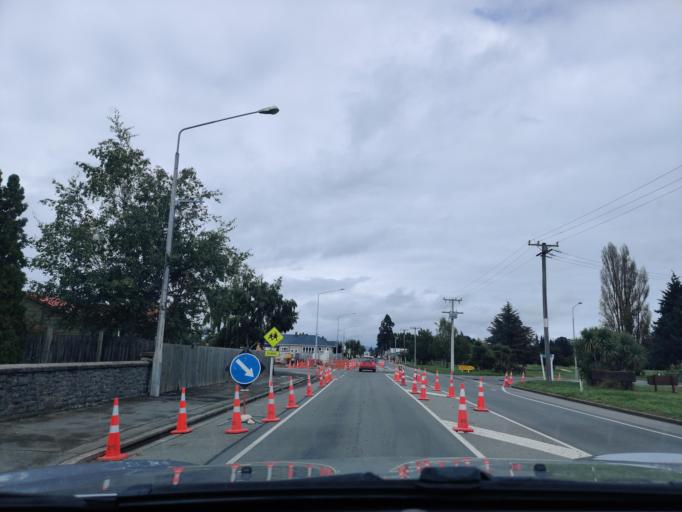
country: NZ
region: Canterbury
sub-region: Hurunui District
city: Amberley
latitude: -42.7722
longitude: 172.8497
